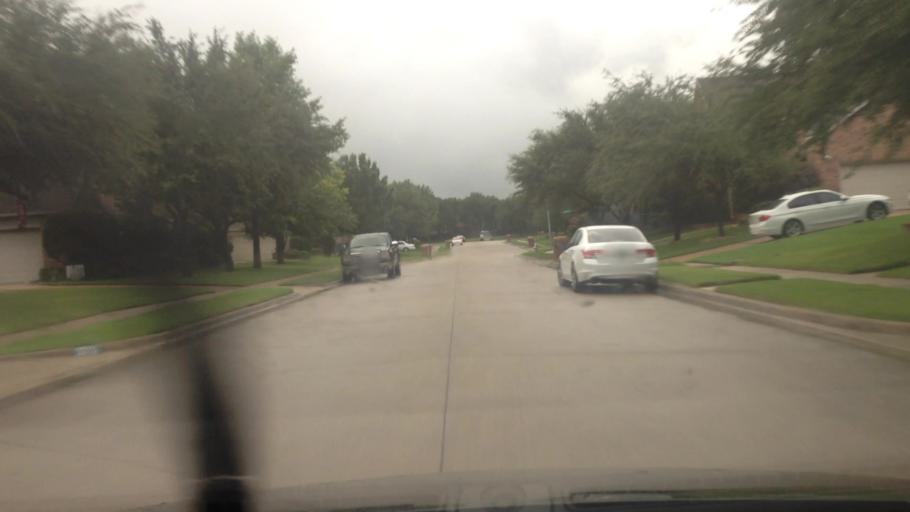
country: US
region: Texas
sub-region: Tarrant County
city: Colleyville
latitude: 32.8824
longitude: -97.1750
